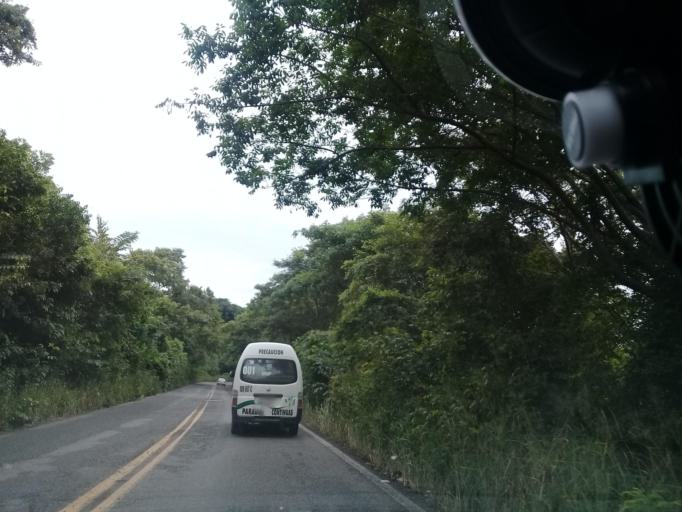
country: MX
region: Veracruz
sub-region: Chalma
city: San Pedro Coyutla
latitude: 21.2007
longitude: -98.3894
